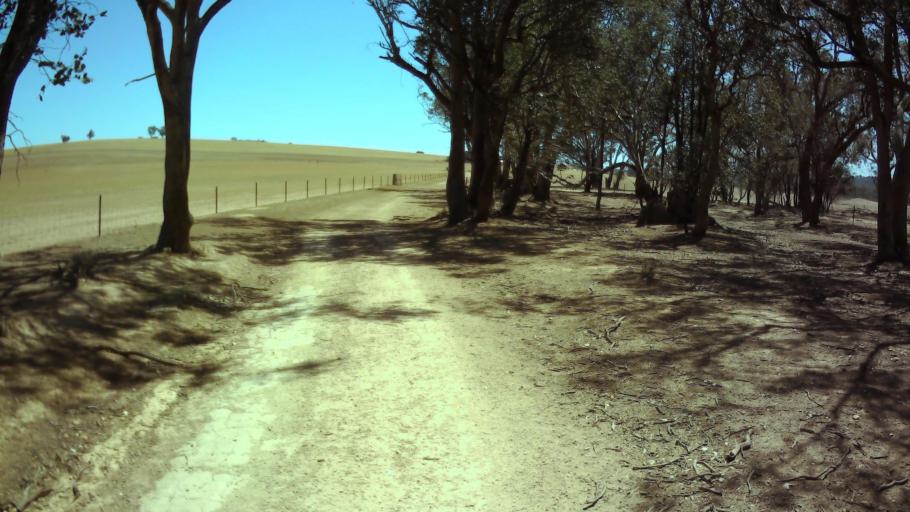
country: AU
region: New South Wales
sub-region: Weddin
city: Grenfell
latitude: -33.9798
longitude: 148.1692
